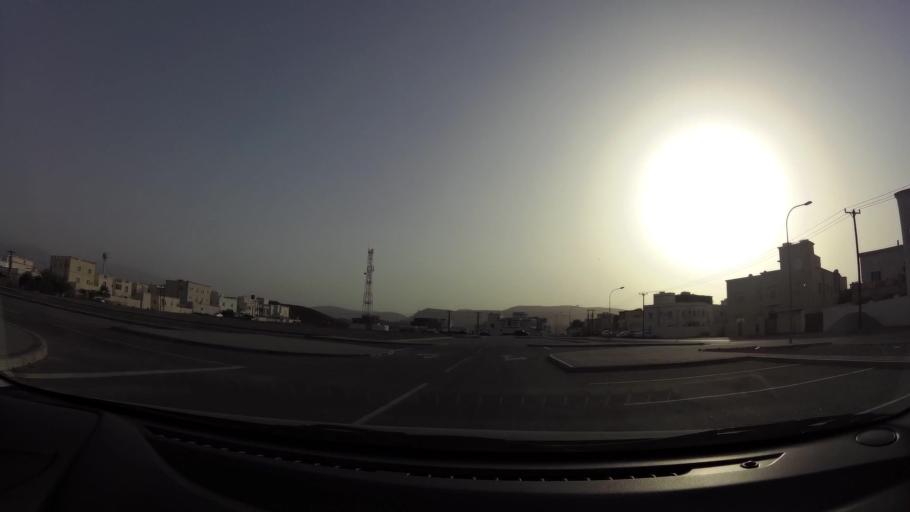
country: OM
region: Muhafazat Masqat
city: Bawshar
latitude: 23.5308
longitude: 58.3490
